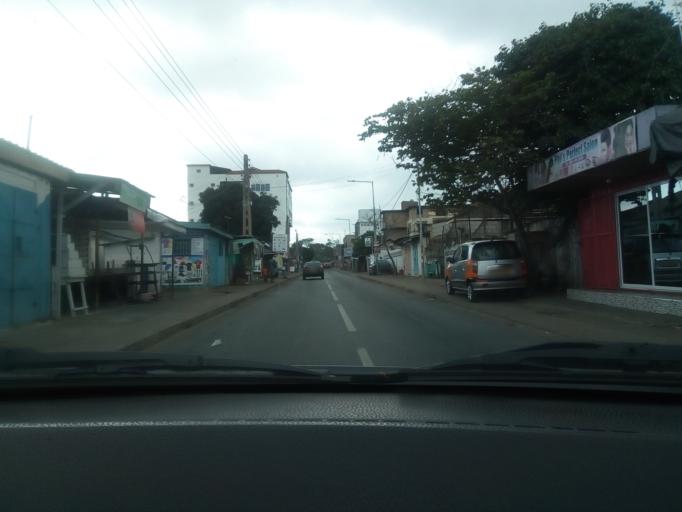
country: GH
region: Greater Accra
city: Accra
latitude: 5.5598
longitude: -0.2115
